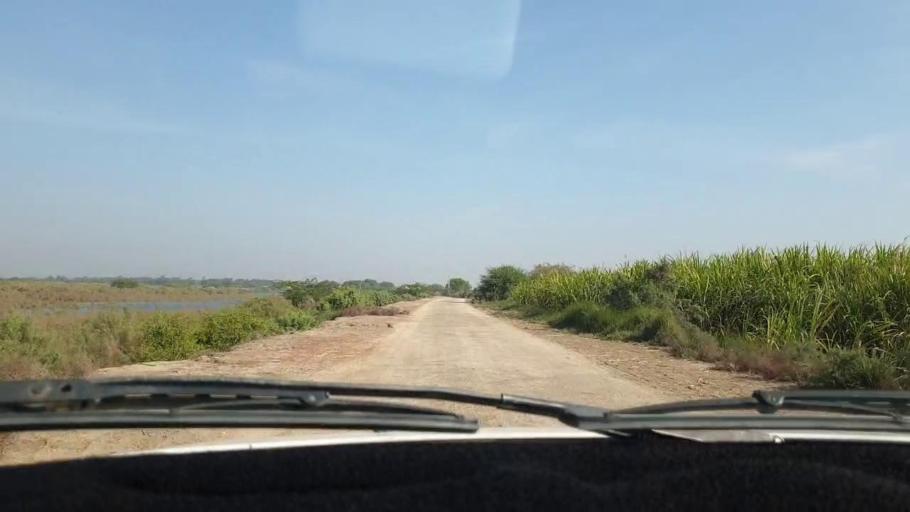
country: PK
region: Sindh
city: Tando Muhammad Khan
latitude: 24.9880
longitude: 68.4626
